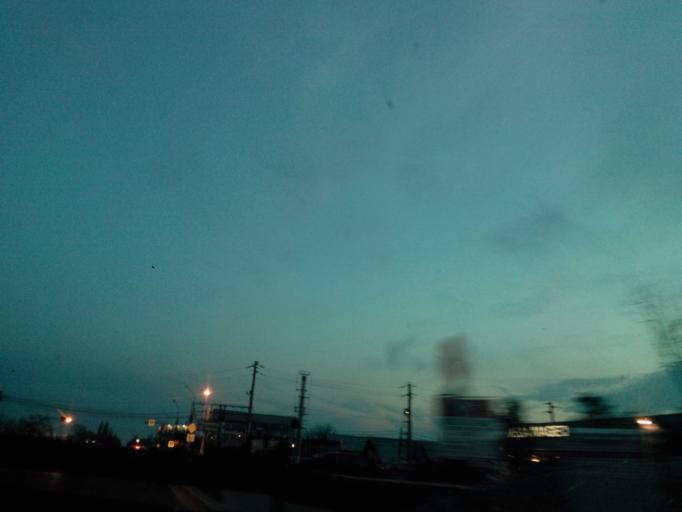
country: RO
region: Ilfov
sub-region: Comuna Corbeanca
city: Corbeanca
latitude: 44.6020
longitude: 26.0716
